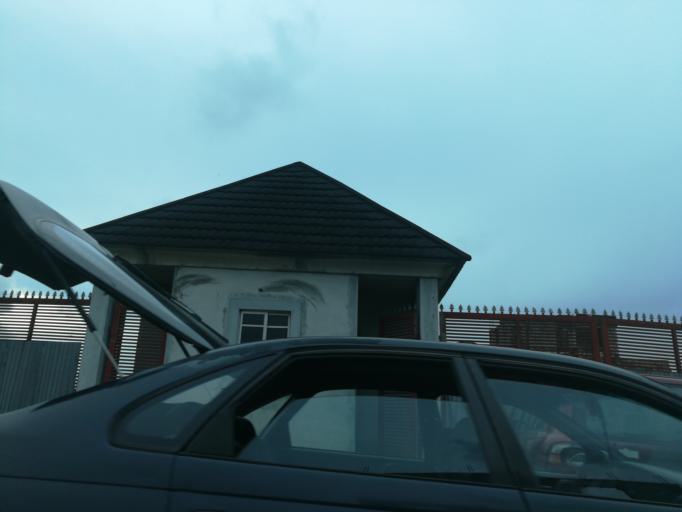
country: NG
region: Rivers
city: Port Harcourt
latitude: 4.8228
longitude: 6.9900
